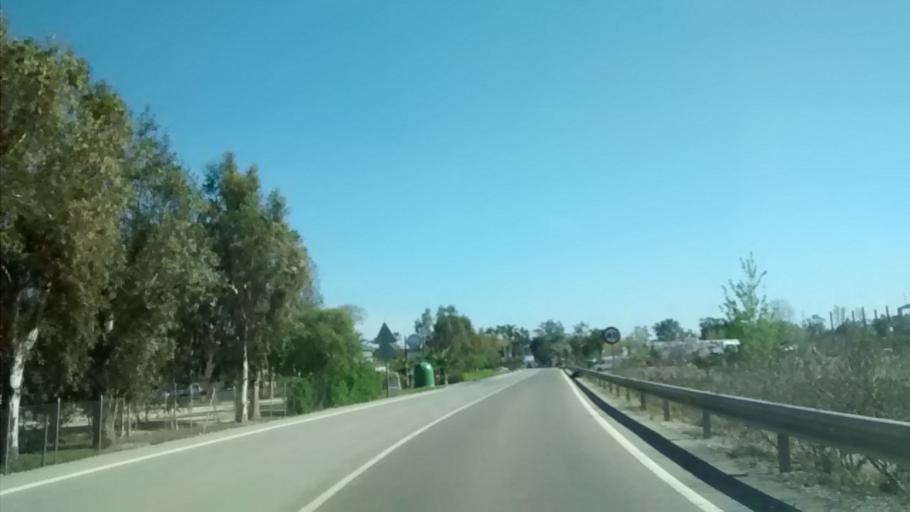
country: ES
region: Catalonia
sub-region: Provincia de Tarragona
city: Deltebre
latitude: 40.7150
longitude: 0.8334
